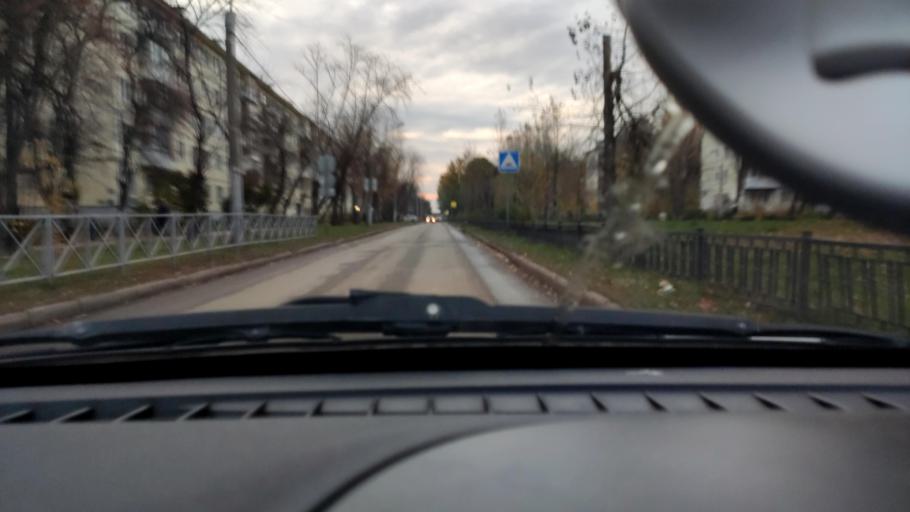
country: RU
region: Perm
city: Perm
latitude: 57.9963
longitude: 56.2960
